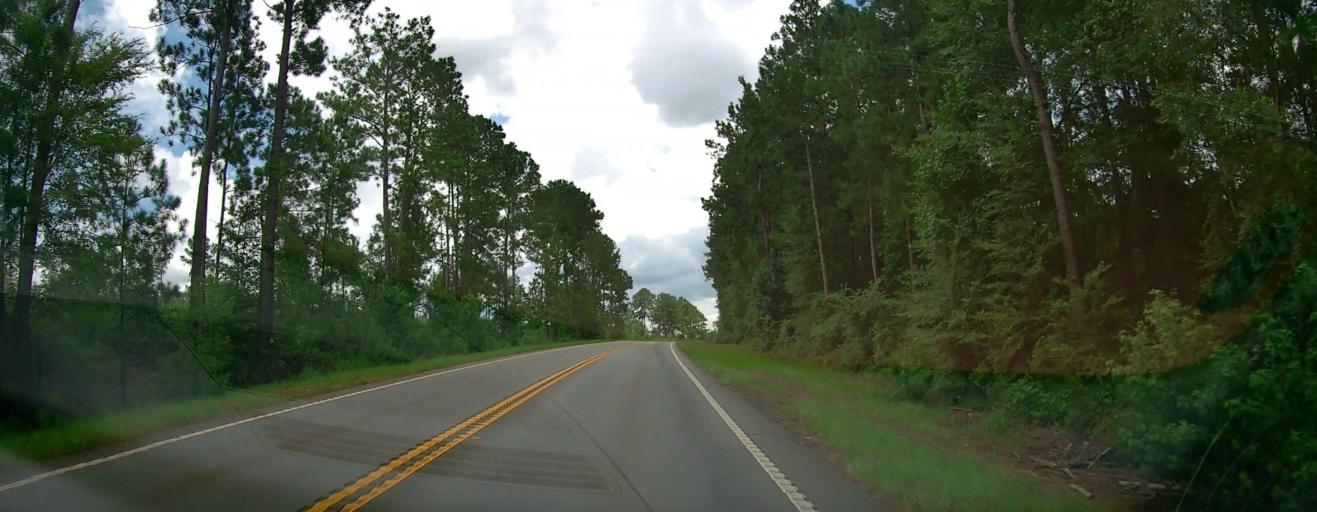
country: US
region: Georgia
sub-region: Pulaski County
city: Hawkinsville
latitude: 32.3755
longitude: -83.5461
